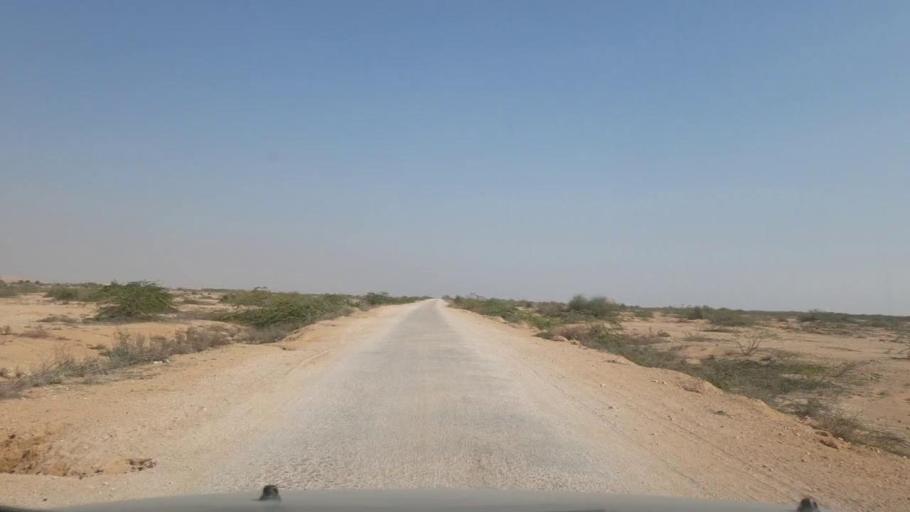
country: PK
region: Sindh
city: Thatta
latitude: 24.9767
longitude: 67.9767
